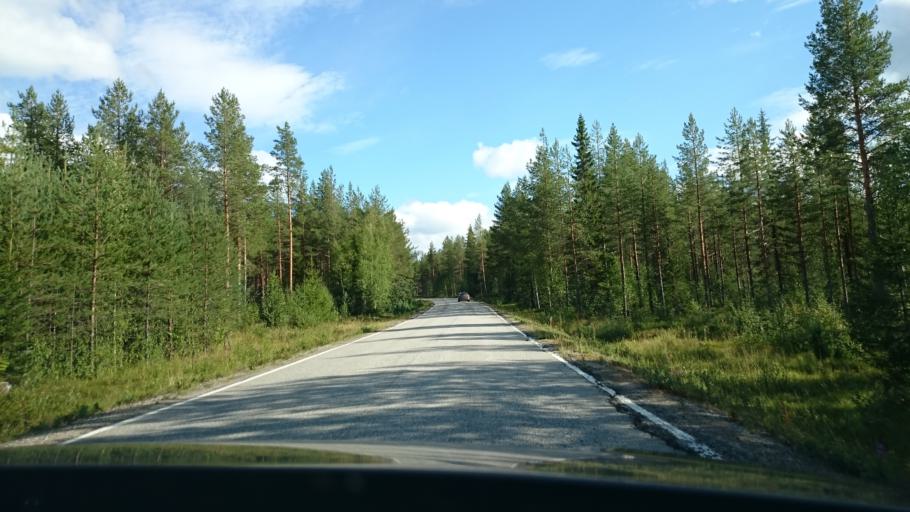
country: FI
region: Kainuu
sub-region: Kehys-Kainuu
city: Suomussalmi
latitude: 64.7534
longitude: 29.4172
